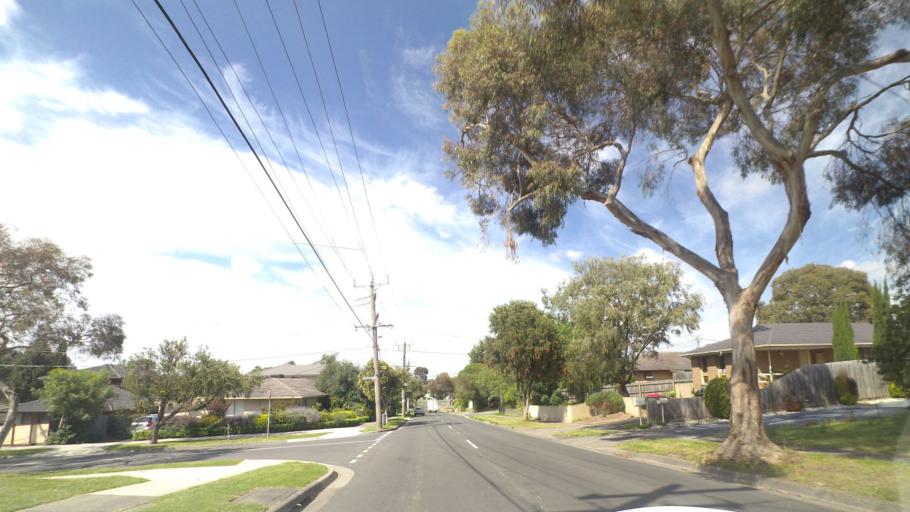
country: AU
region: Victoria
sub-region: Knox
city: Bayswater
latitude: -37.8537
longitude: 145.2525
